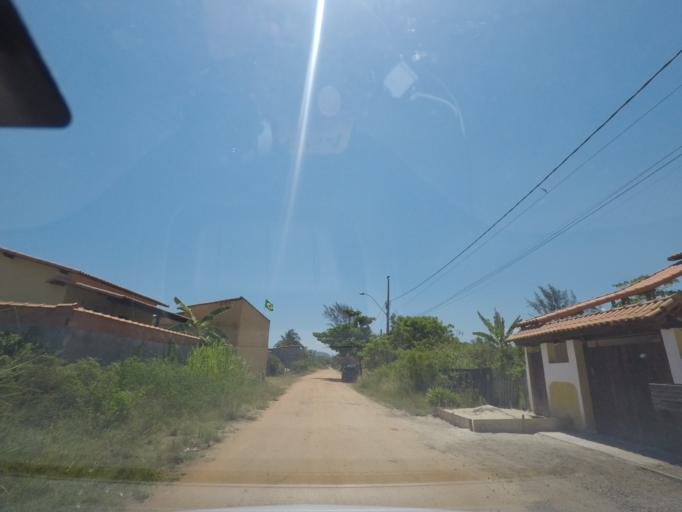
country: BR
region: Rio de Janeiro
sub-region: Marica
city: Marica
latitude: -22.9706
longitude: -42.9415
